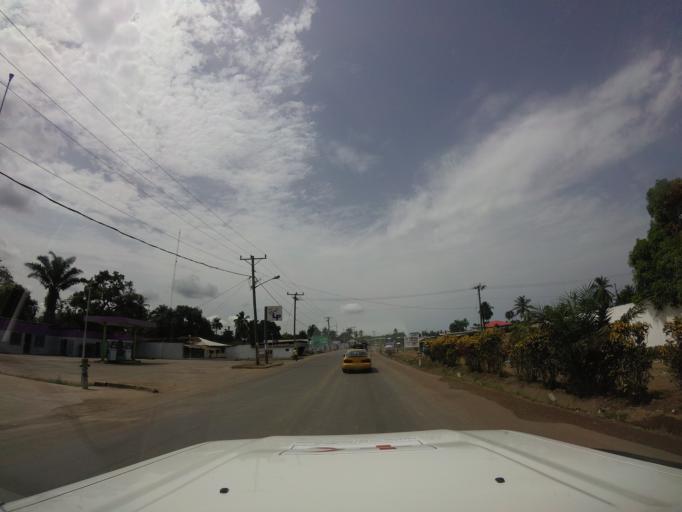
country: LR
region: Montserrado
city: Monrovia
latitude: 6.3808
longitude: -10.7824
